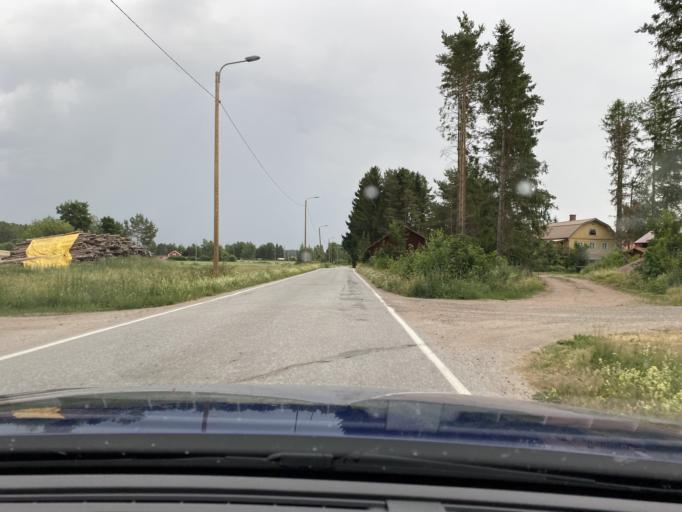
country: FI
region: Satakunta
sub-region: Rauma
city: Eura
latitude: 61.1485
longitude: 22.1243
